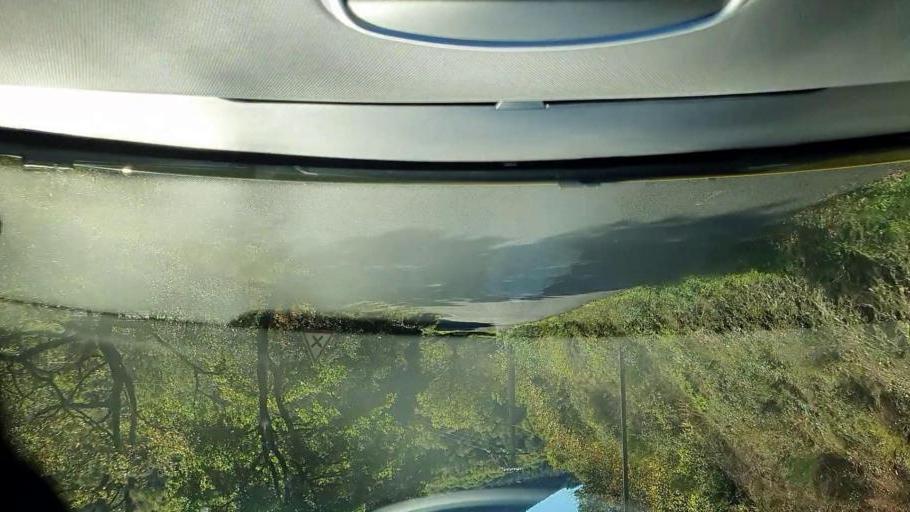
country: FR
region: Languedoc-Roussillon
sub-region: Departement du Gard
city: Le Vigan
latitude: 43.9782
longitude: 3.4969
